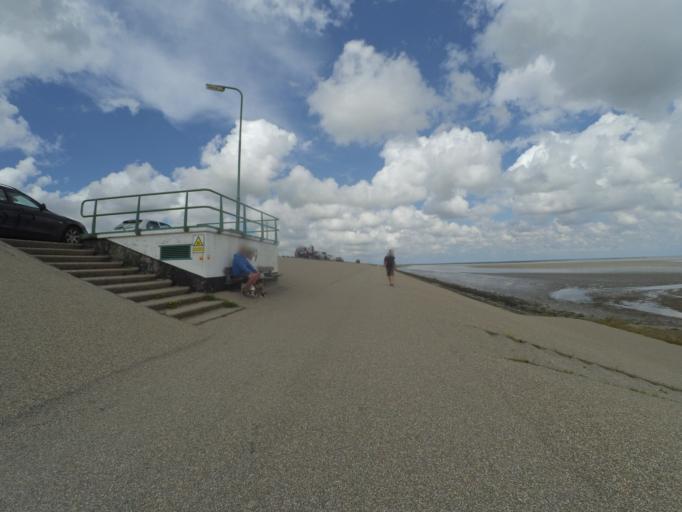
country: NL
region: North Holland
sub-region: Gemeente Texel
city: Den Burg
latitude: 53.0999
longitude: 4.8981
